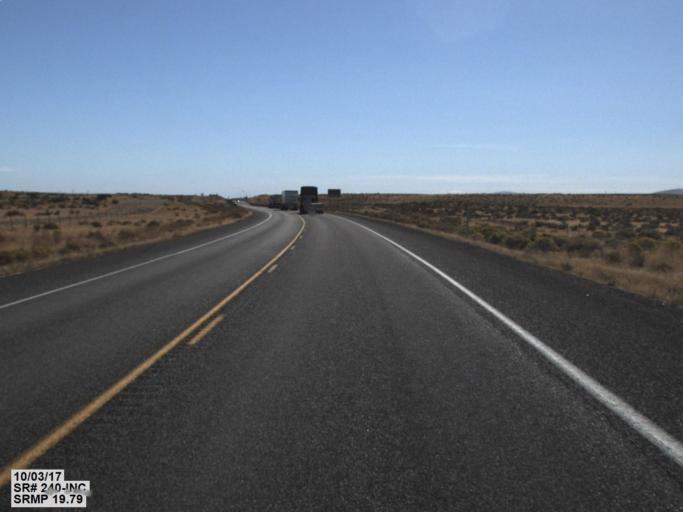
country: US
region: Washington
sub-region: Benton County
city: West Richland
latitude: 46.3895
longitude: -119.4341
